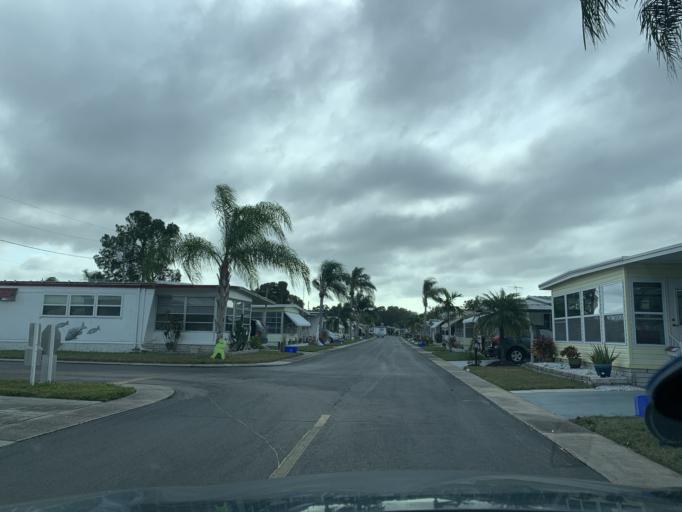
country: US
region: Florida
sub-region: Pinellas County
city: Largo
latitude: 27.8888
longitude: -82.7792
